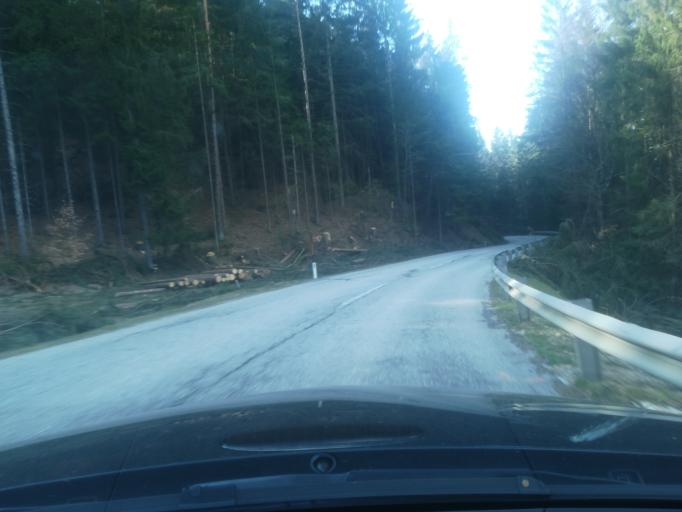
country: AT
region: Upper Austria
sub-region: Politischer Bezirk Freistadt
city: Freistadt
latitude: 48.4382
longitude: 14.6625
